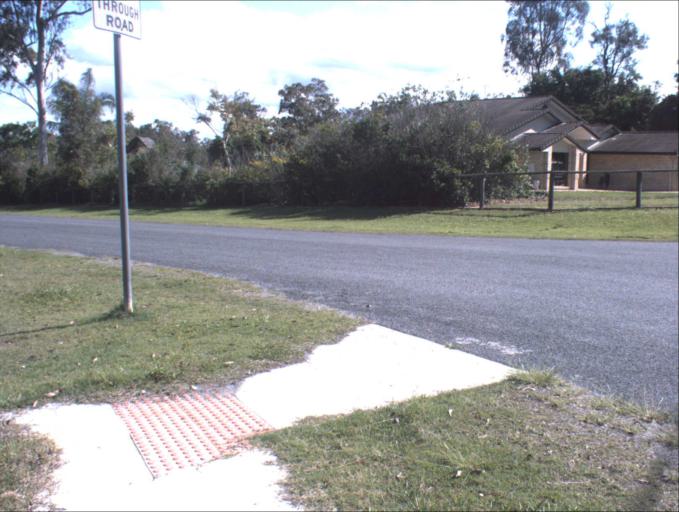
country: AU
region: Queensland
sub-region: Logan
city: Park Ridge South
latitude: -27.7436
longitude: 153.0369
